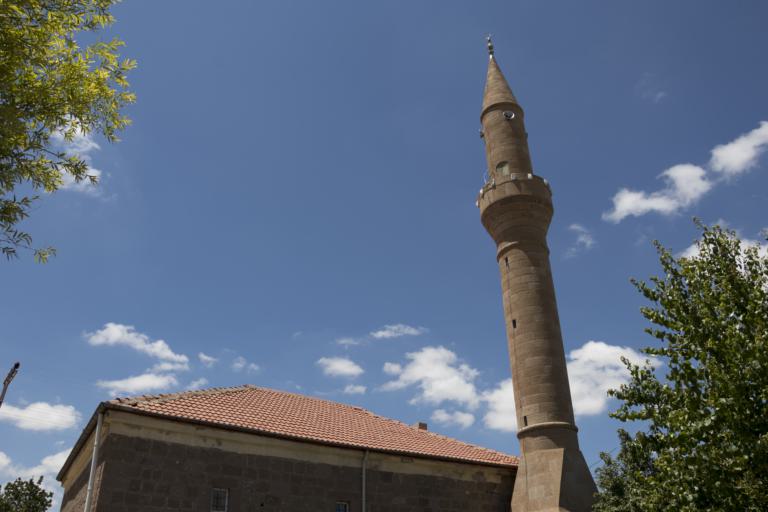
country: TR
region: Kayseri
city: Toklar
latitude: 38.4211
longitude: 36.0944
